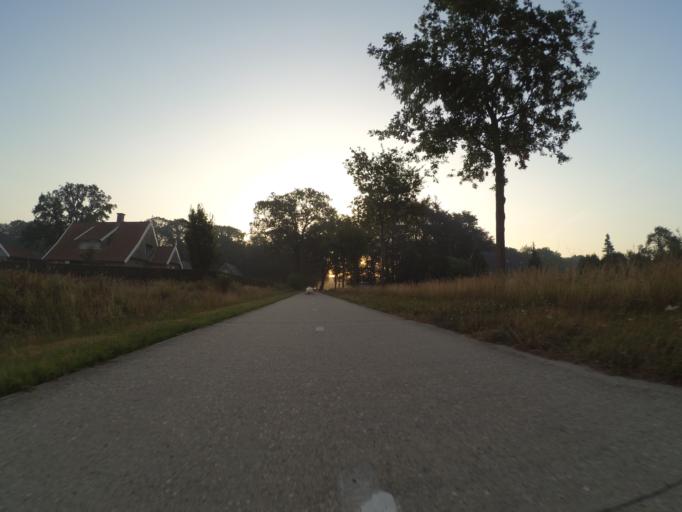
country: NL
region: Overijssel
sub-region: Gemeente Tubbergen
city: Tubbergen
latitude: 52.3944
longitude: 6.7499
